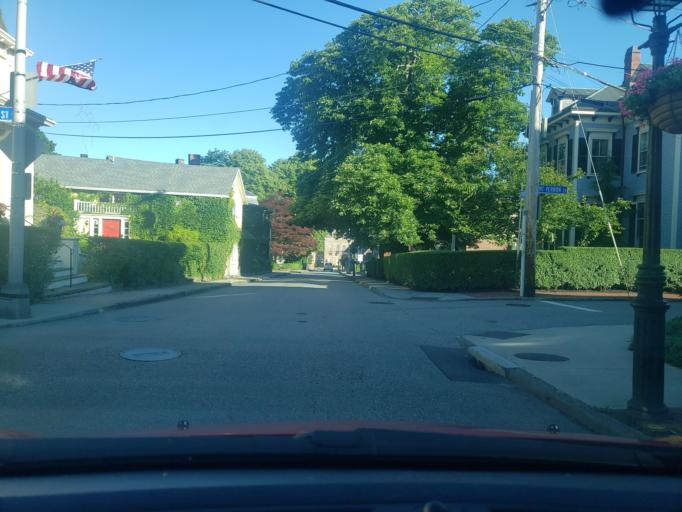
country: US
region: Rhode Island
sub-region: Newport County
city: Newport
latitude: 41.4887
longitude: -71.3111
